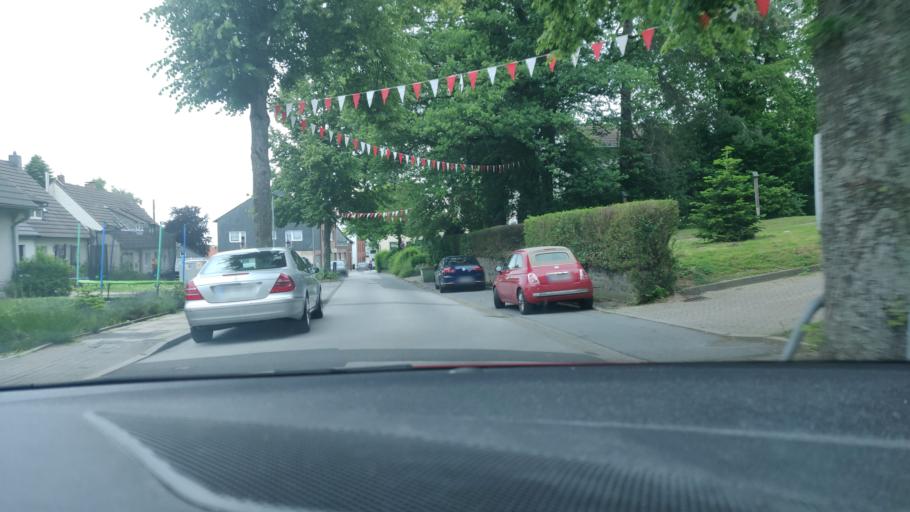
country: DE
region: North Rhine-Westphalia
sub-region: Regierungsbezirk Dusseldorf
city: Heiligenhaus
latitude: 51.2972
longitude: 6.9205
